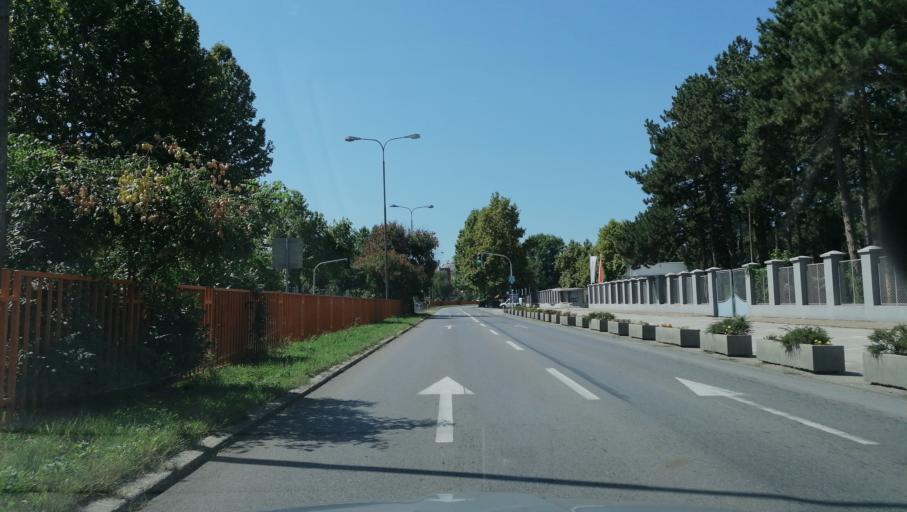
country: RS
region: Central Serbia
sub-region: Kolubarski Okrug
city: Valjevo
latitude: 44.2745
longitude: 19.9070
